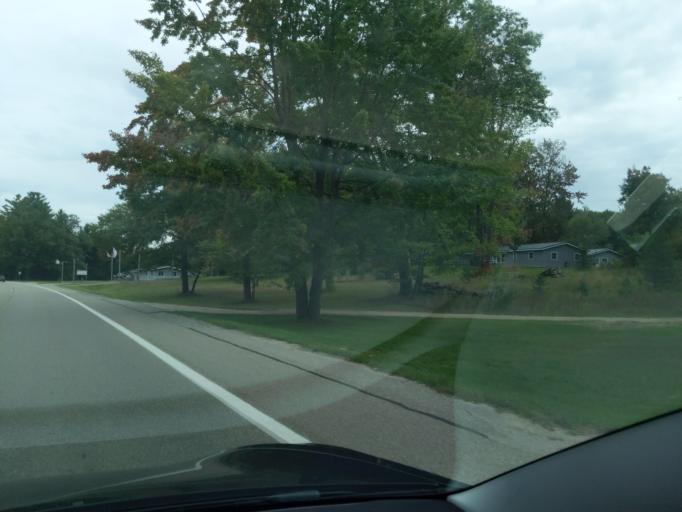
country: US
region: Michigan
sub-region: Clare County
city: Clare
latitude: 43.8396
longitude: -84.8829
